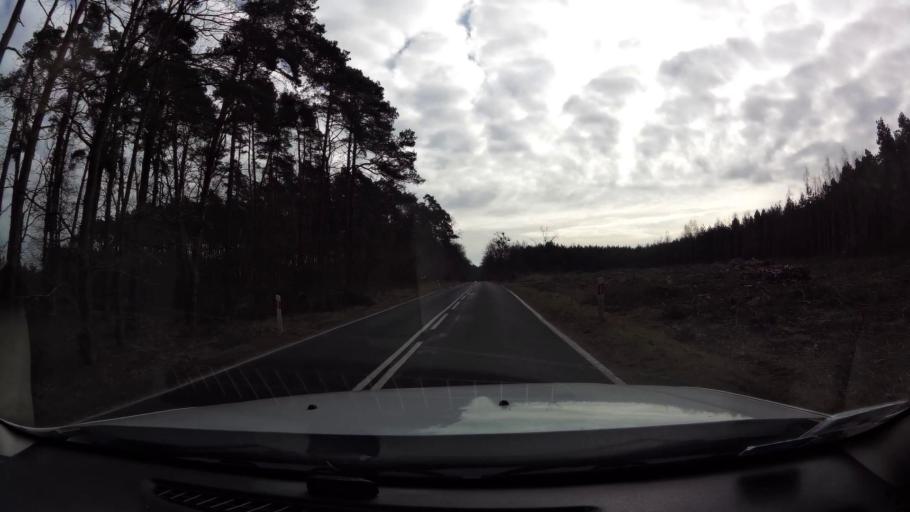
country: PL
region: West Pomeranian Voivodeship
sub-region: Powiat mysliborski
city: Debno
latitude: 52.7702
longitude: 14.6669
